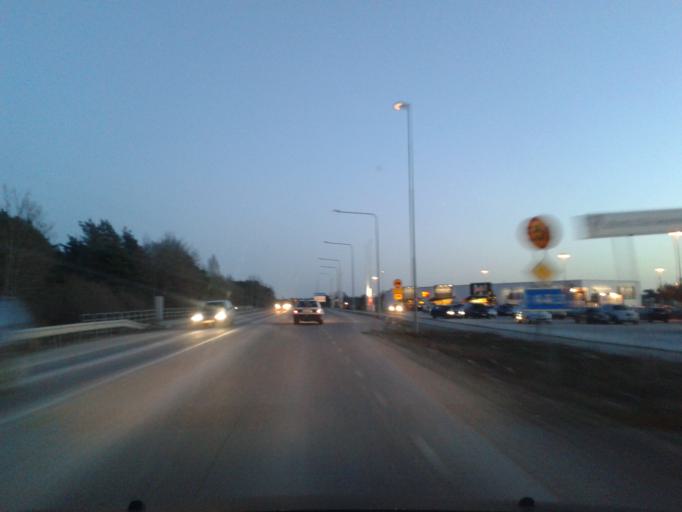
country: SE
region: Gotland
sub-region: Gotland
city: Visby
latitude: 57.6246
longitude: 18.3228
